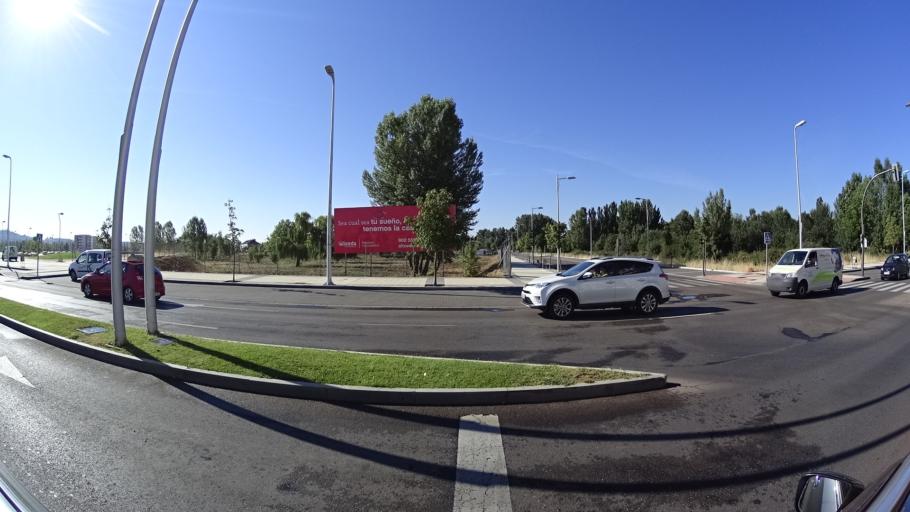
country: ES
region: Castille and Leon
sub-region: Provincia de Leon
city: Leon
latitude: 42.5814
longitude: -5.5667
